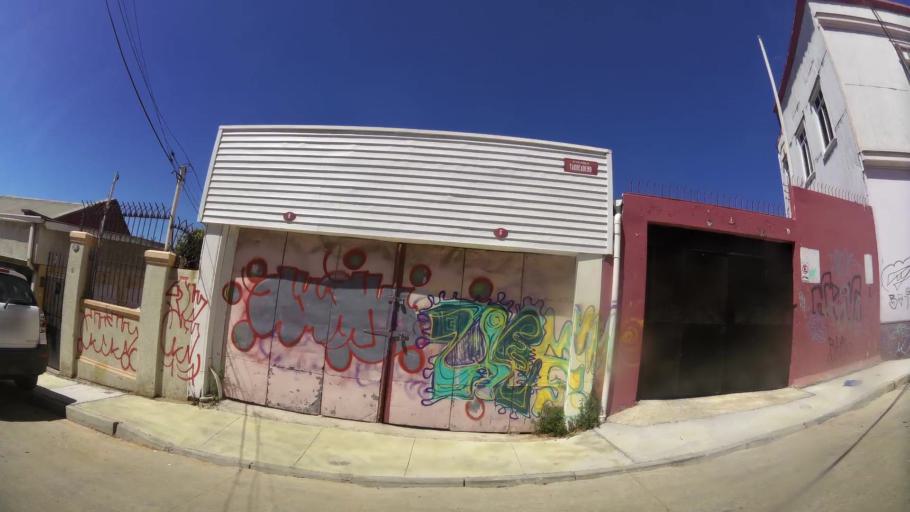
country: CL
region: Valparaiso
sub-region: Provincia de Valparaiso
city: Valparaiso
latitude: -33.0307
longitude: -71.6333
